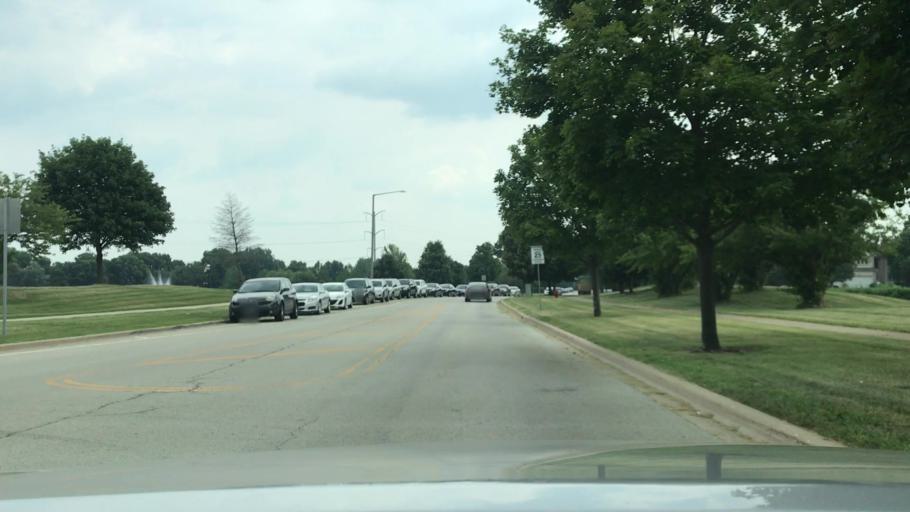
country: US
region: Illinois
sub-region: Will County
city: Plainfield
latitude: 41.6071
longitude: -88.2153
